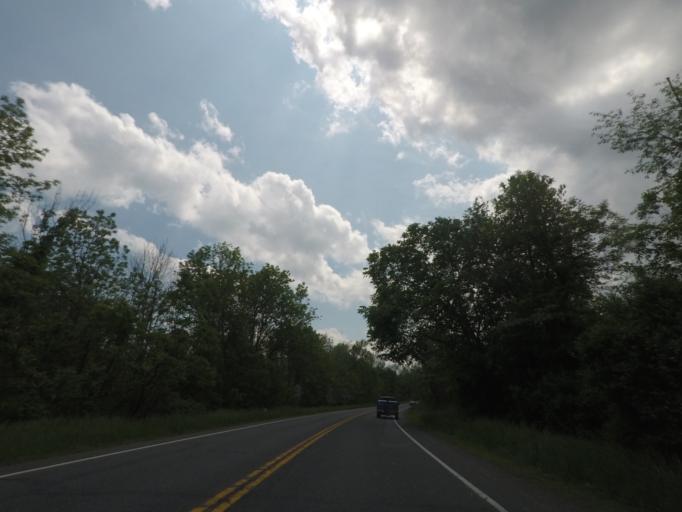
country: US
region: New York
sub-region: Columbia County
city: Stottville
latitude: 42.3094
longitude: -73.7023
